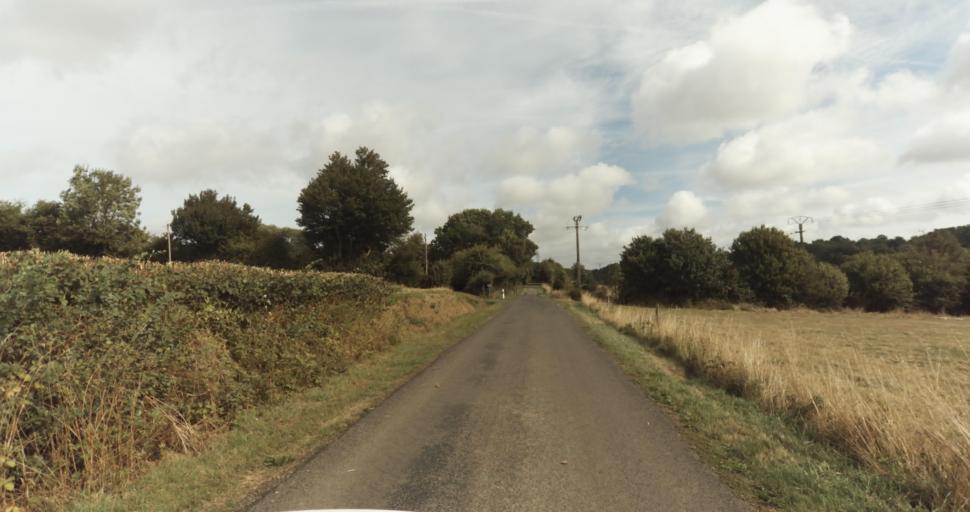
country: FR
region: Lower Normandy
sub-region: Departement de l'Orne
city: Gace
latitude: 48.8438
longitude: 0.3875
